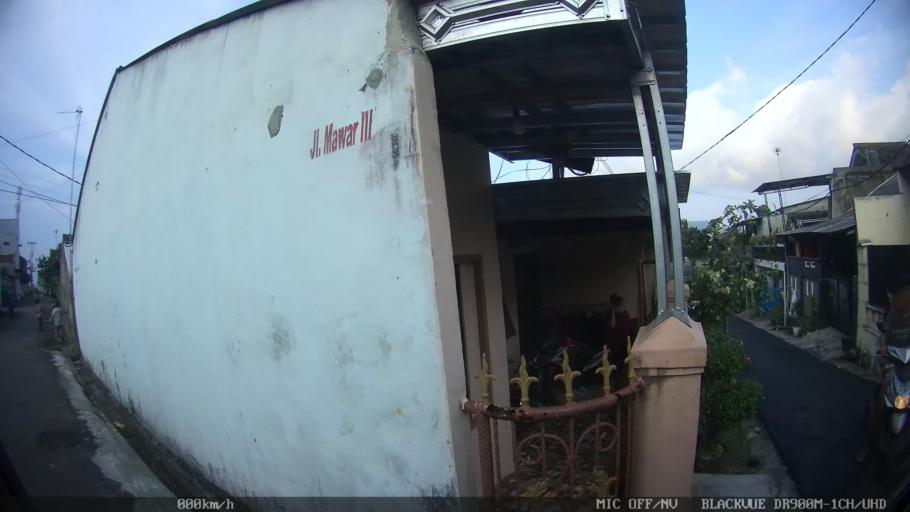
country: ID
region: Lampung
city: Kedaton
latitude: -5.4026
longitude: 105.2944
